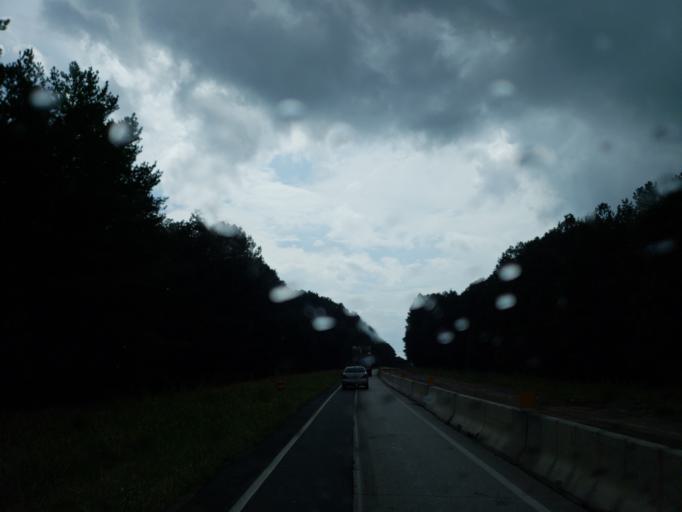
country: US
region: Georgia
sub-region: Carroll County
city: Temple
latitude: 33.7005
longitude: -85.0650
